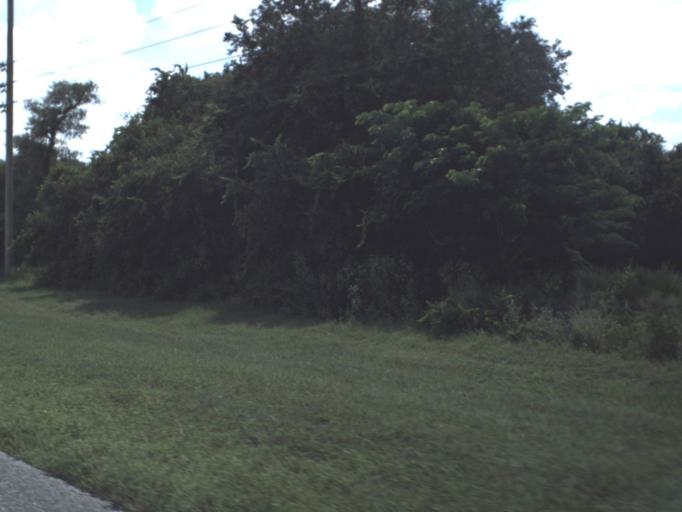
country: US
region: Florida
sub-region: Polk County
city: Crooked Lake Park
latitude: 27.8631
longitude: -81.5900
